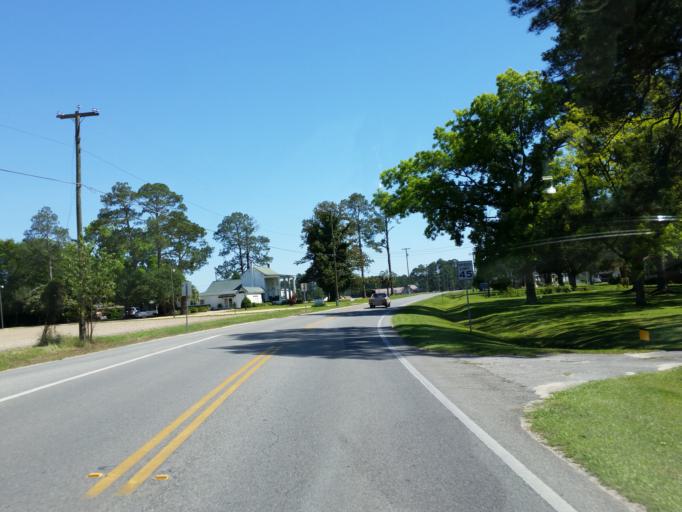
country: US
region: Georgia
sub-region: Cook County
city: Adel
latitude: 31.1202
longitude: -83.4156
